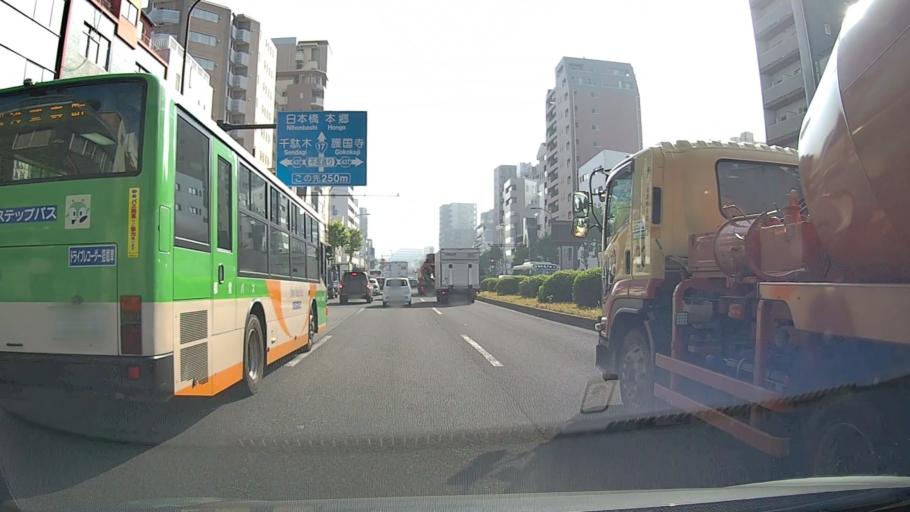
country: JP
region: Tokyo
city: Tokyo
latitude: 35.7308
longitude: 139.7417
